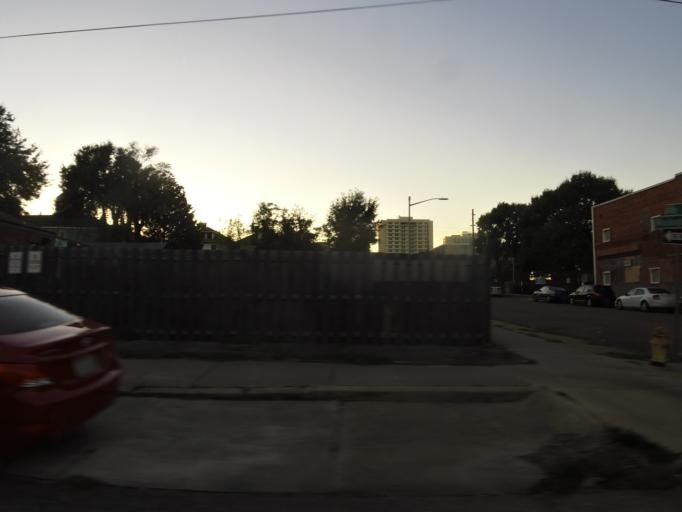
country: US
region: Florida
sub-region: Duval County
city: Jacksonville
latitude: 30.3293
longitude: -81.6504
